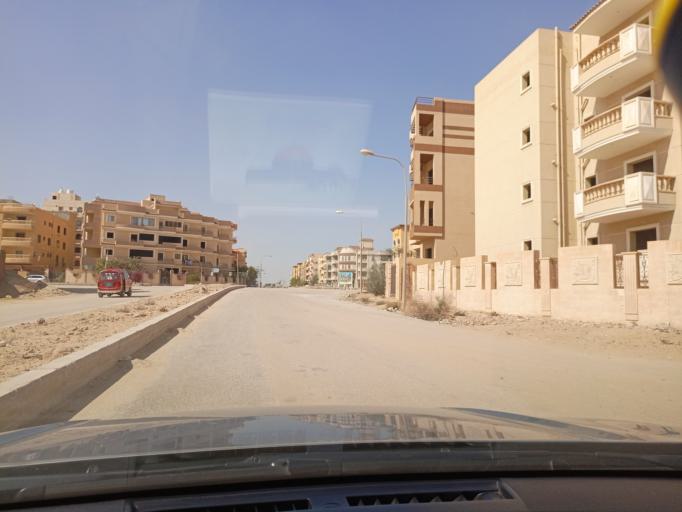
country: EG
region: Muhafazat al Qalyubiyah
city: Al Khankah
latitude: 30.2211
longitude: 31.4420
